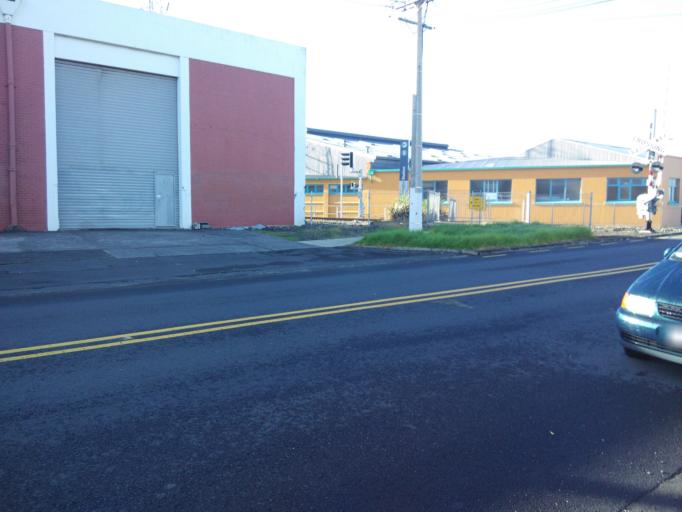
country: NZ
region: Auckland
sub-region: Auckland
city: Mangere
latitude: -36.9207
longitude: 174.8001
